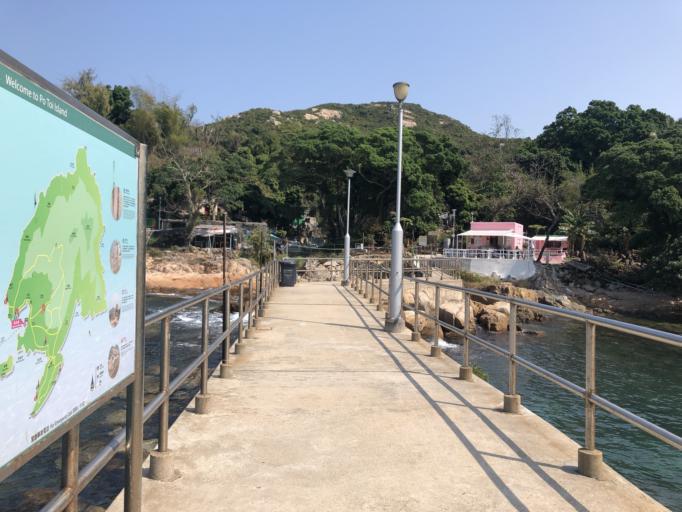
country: HK
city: Sok Kwu Wan
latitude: 22.1633
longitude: 114.2532
